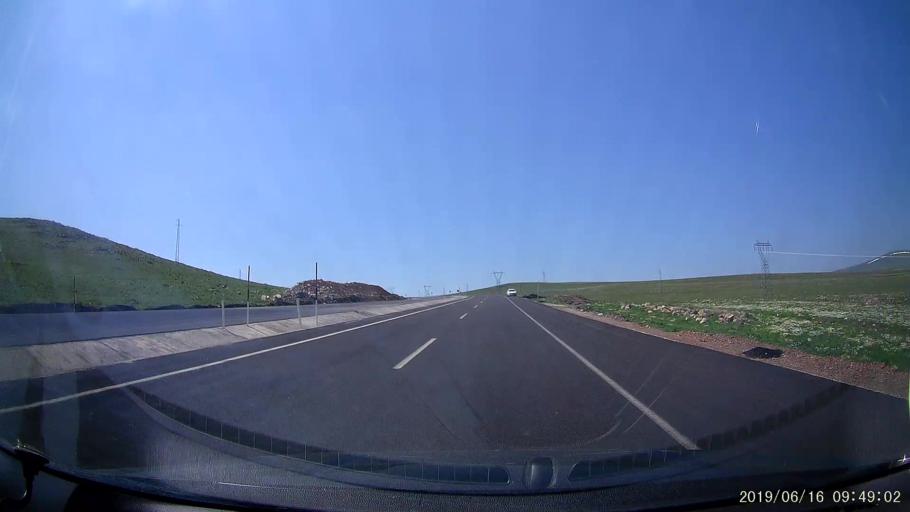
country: TR
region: Kars
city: Digor
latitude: 40.4262
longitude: 43.3563
